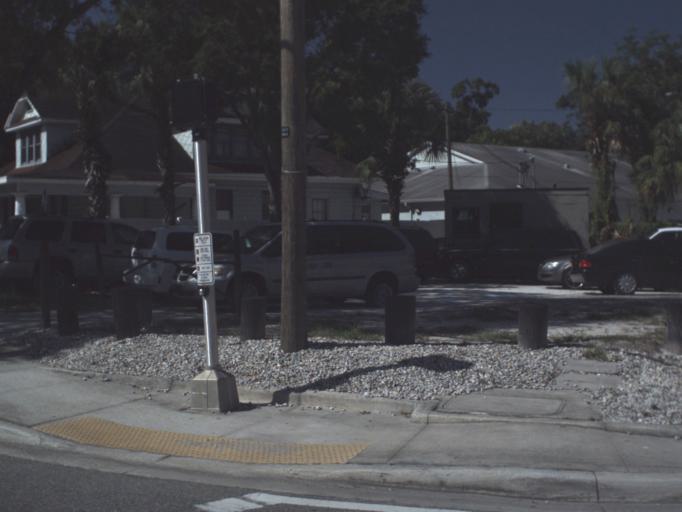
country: US
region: Florida
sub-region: Hillsborough County
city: Egypt Lake-Leto
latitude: 28.0106
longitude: -82.4514
